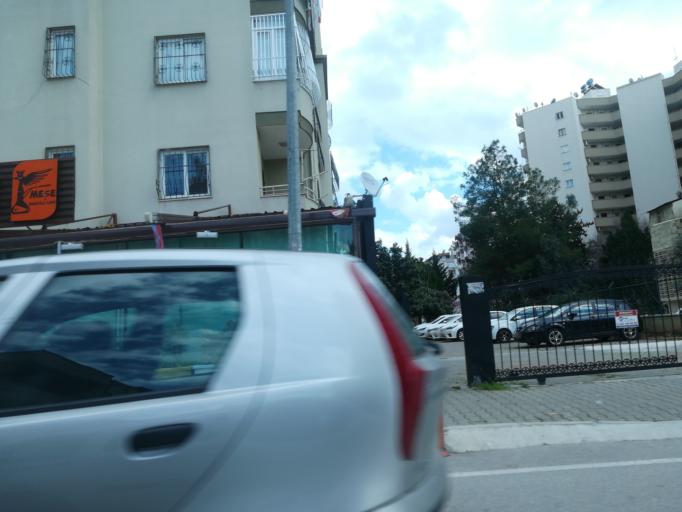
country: TR
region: Adana
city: Adana
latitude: 37.0359
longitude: 35.3126
